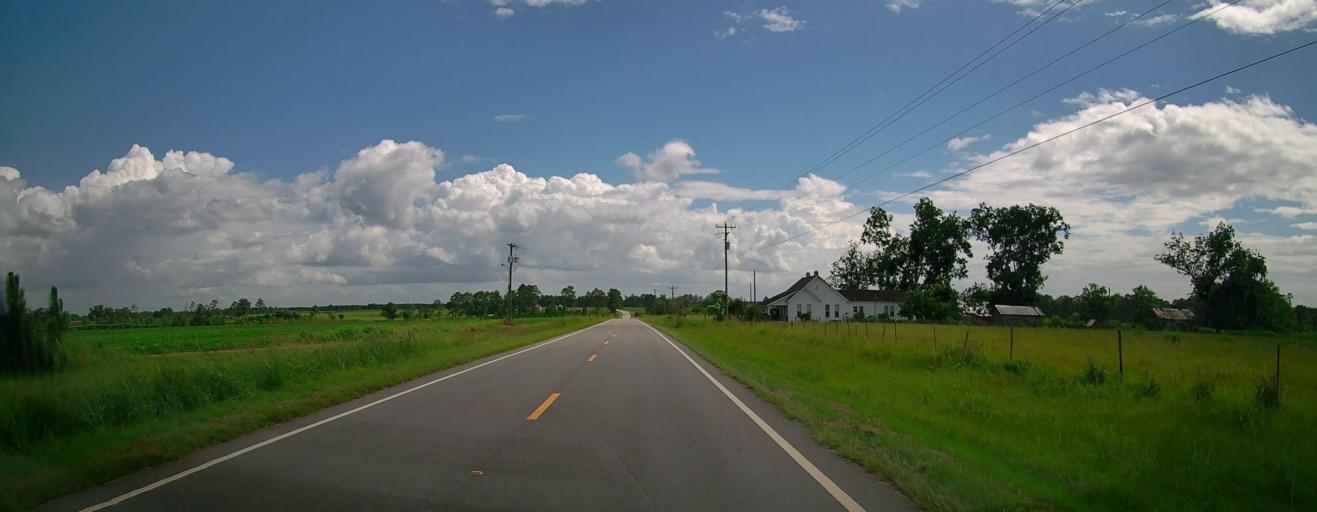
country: US
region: Georgia
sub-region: Irwin County
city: Ocilla
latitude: 31.6134
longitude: -83.1656
